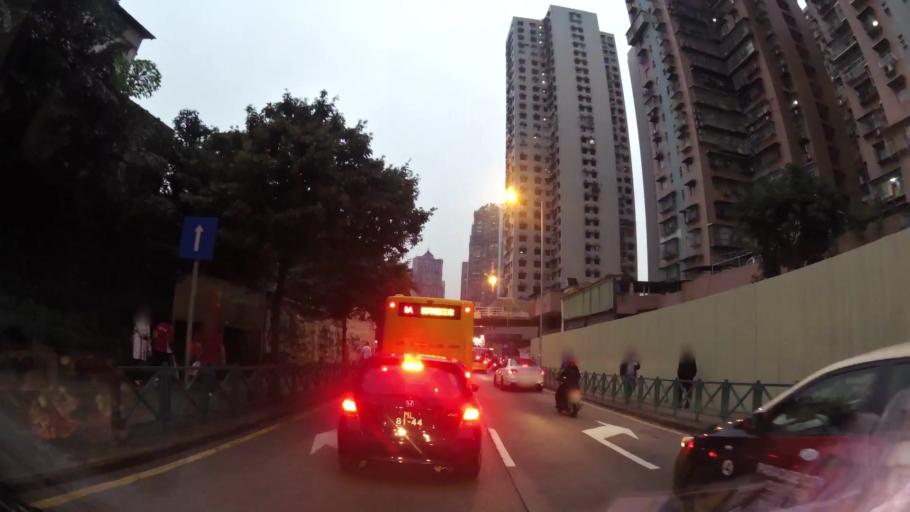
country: MO
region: Macau
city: Macau
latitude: 22.2103
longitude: 113.5480
